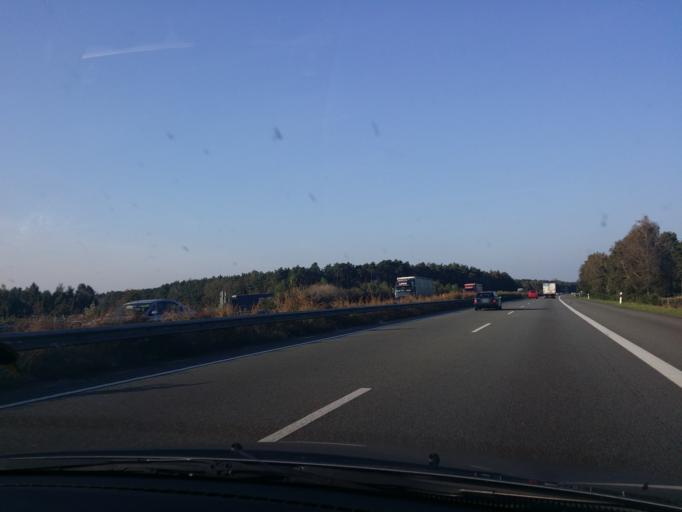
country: DE
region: Lower Saxony
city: Bramsche
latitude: 52.4219
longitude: 8.0312
